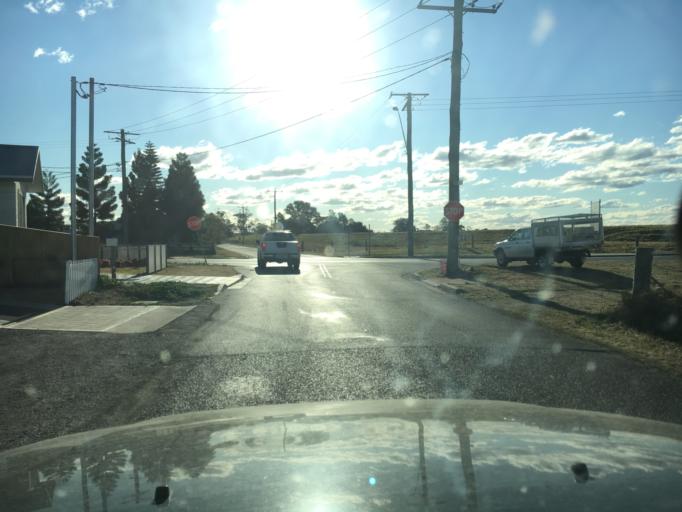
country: AU
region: New South Wales
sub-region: Maitland Municipality
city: Bolwarra
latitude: -32.7238
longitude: 151.5650
